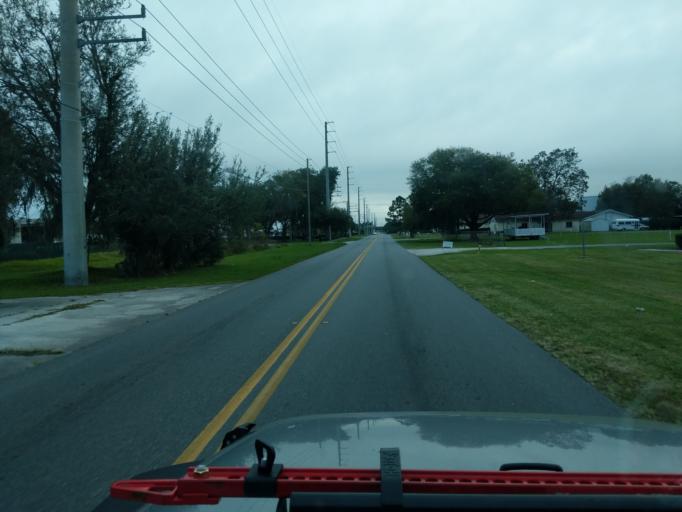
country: US
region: Florida
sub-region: Orange County
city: Winter Garden
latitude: 28.5585
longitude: -81.5680
